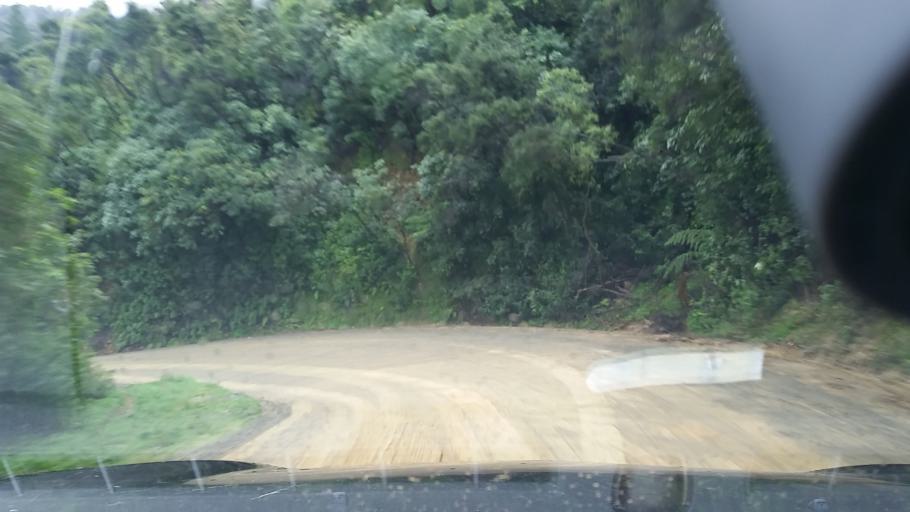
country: NZ
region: Marlborough
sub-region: Marlborough District
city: Picton
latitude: -41.3773
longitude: 174.0569
